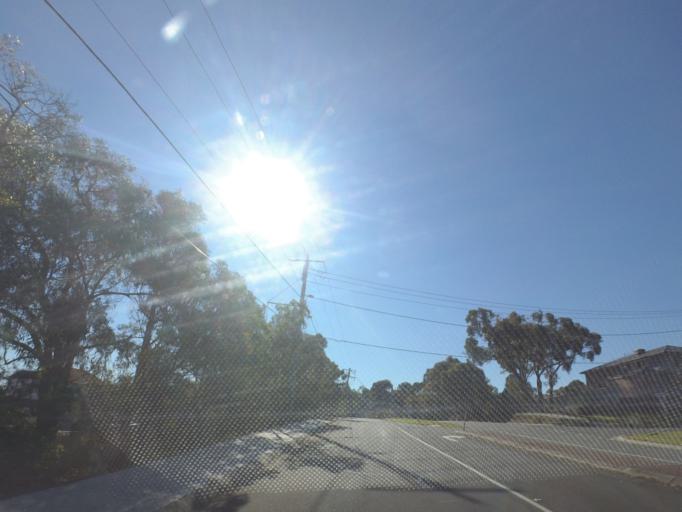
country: AU
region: Victoria
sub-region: Maroondah
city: Croydon Hills
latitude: -37.7662
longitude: 145.2717
